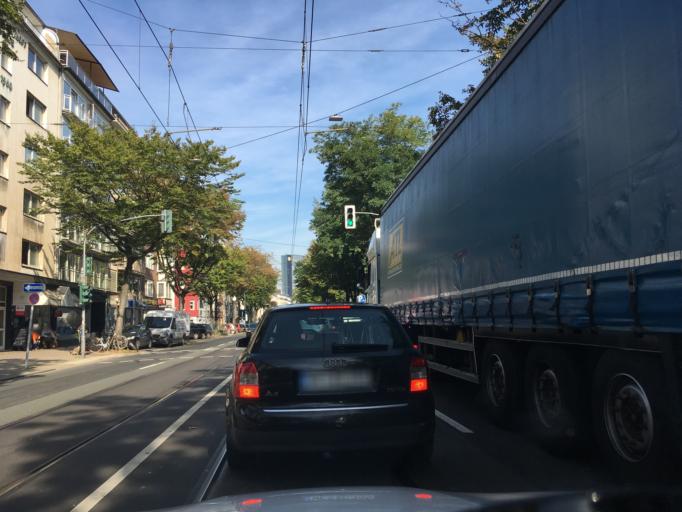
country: DE
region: North Rhine-Westphalia
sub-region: Regierungsbezirk Dusseldorf
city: Dusseldorf
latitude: 51.2404
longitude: 6.8023
